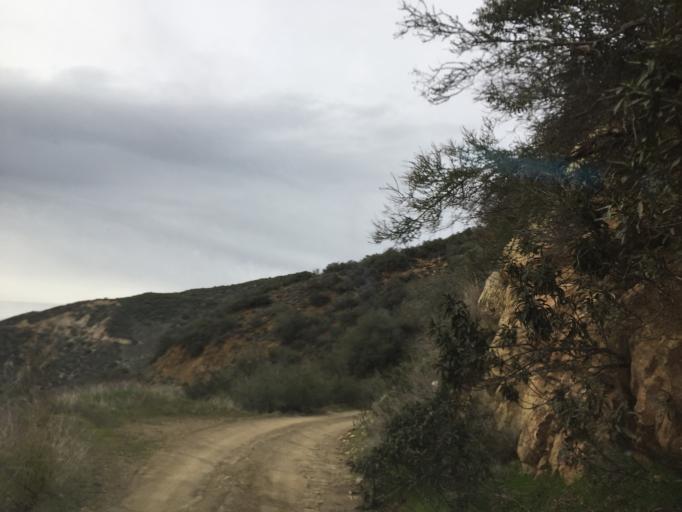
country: US
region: California
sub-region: San Bernardino County
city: Yucaipa
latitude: 34.1100
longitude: -117.0340
